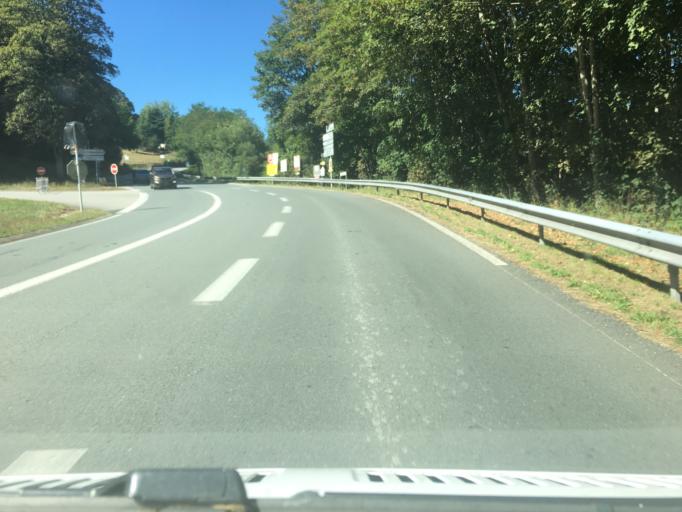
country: FR
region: Limousin
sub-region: Departement de la Correze
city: Bort-les-Orgues
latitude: 45.4172
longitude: 2.5019
